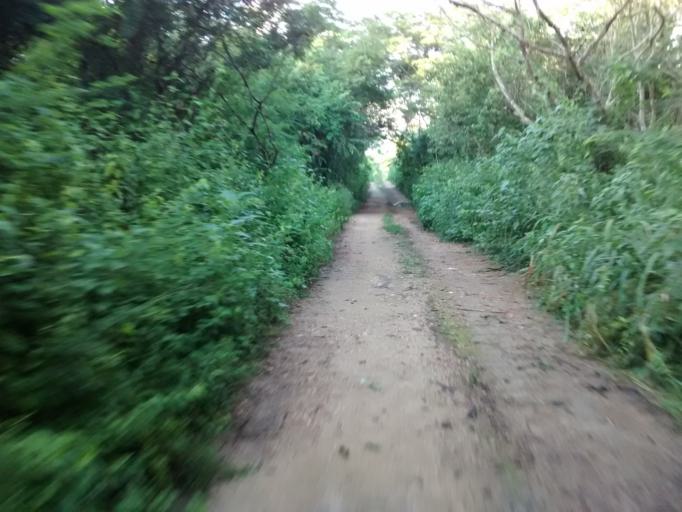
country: MX
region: Yucatan
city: Valladolid
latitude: 20.7139
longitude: -88.2068
